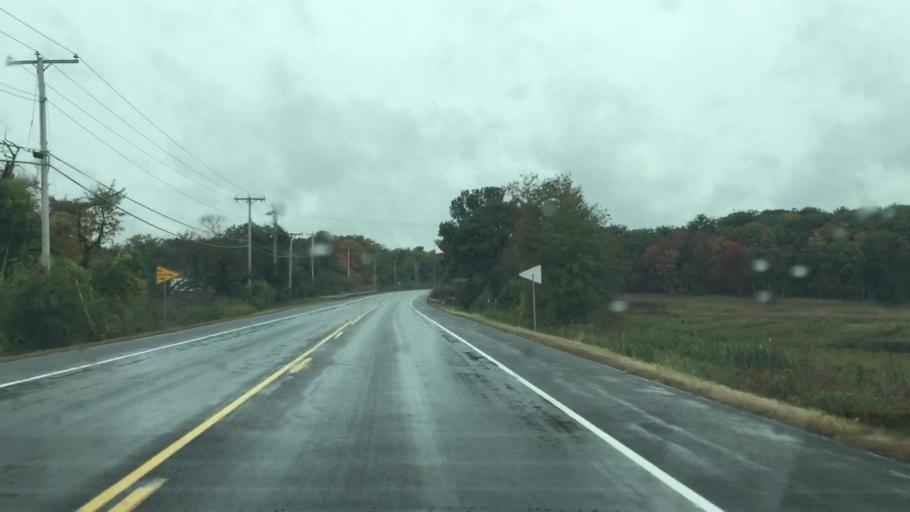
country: US
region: Massachusetts
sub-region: Essex County
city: Salisbury
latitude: 42.8698
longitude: -70.8379
